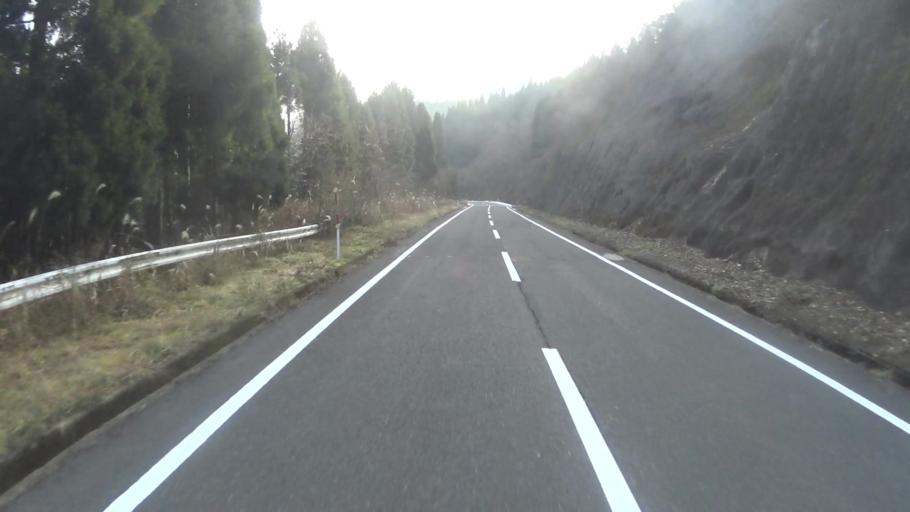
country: JP
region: Kyoto
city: Maizuru
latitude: 35.4196
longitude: 135.4095
